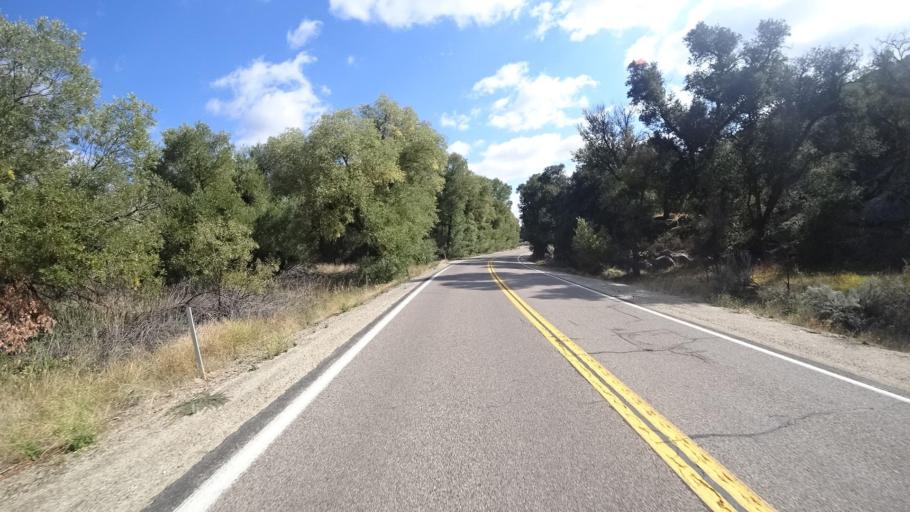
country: US
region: California
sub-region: San Diego County
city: Campo
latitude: 32.7113
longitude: -116.4933
